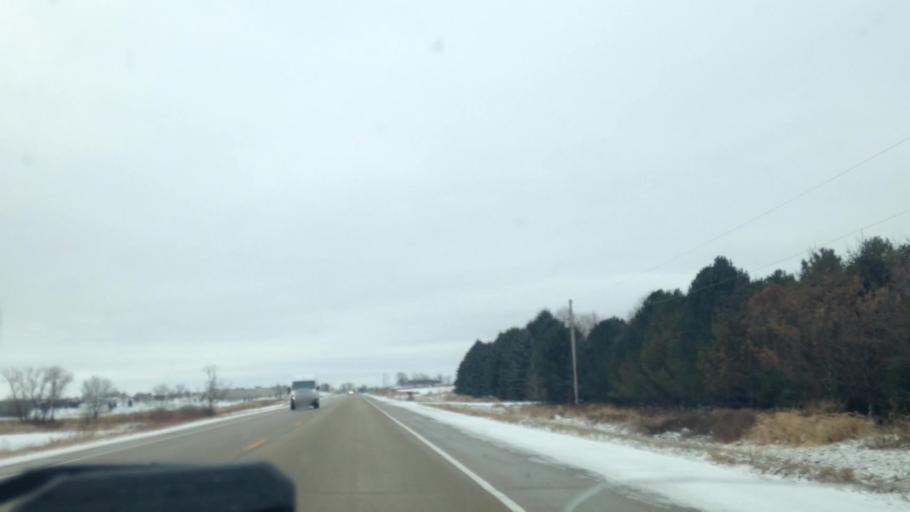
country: US
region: Wisconsin
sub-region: Dodge County
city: Mayville
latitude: 43.4884
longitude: -88.5778
